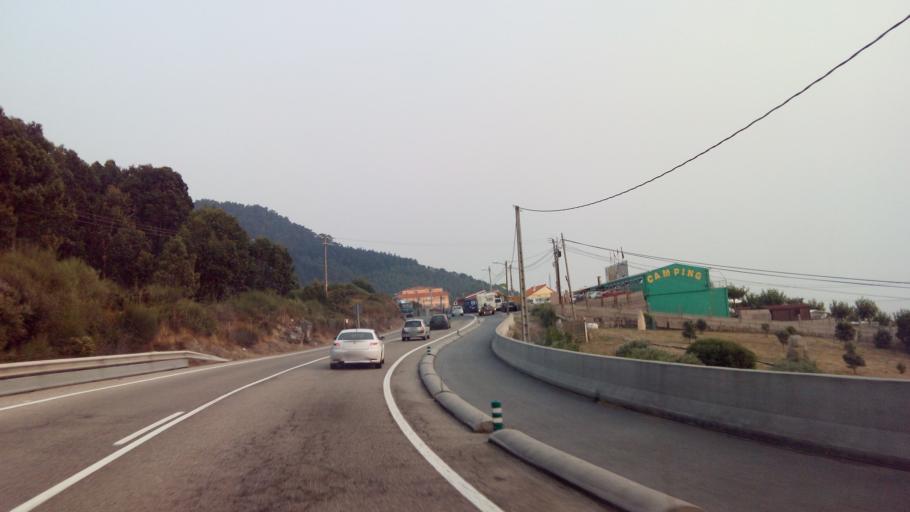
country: ES
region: Galicia
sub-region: Provincia de Pontevedra
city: Baiona
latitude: 42.0875
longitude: -8.8912
